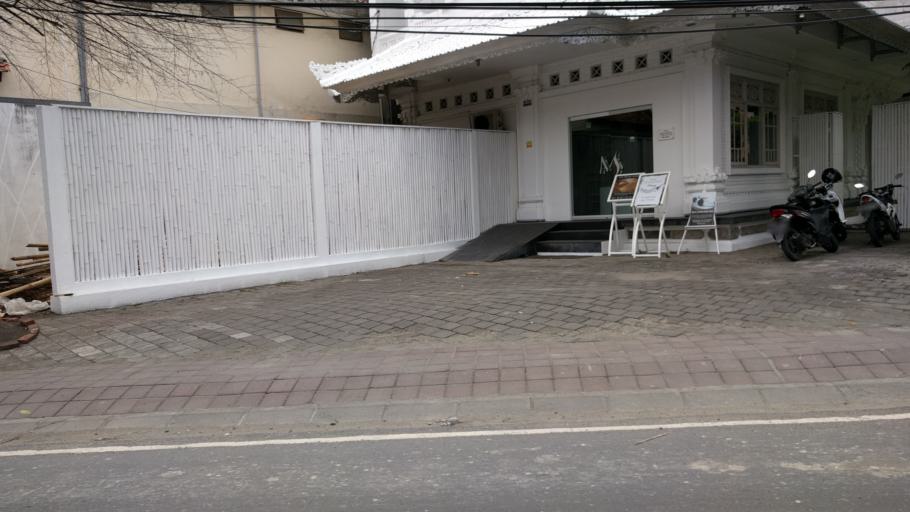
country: ID
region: Bali
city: Kuta
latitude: -8.6731
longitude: 115.1586
